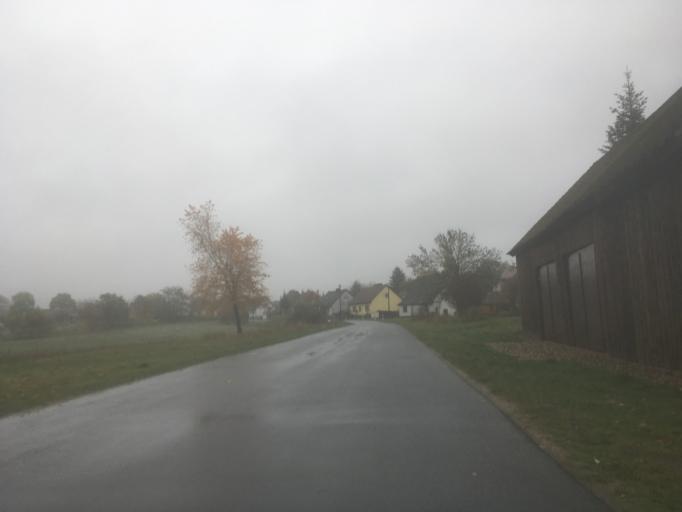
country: DE
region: Brandenburg
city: Schlepzig
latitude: 52.0225
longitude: 13.9806
